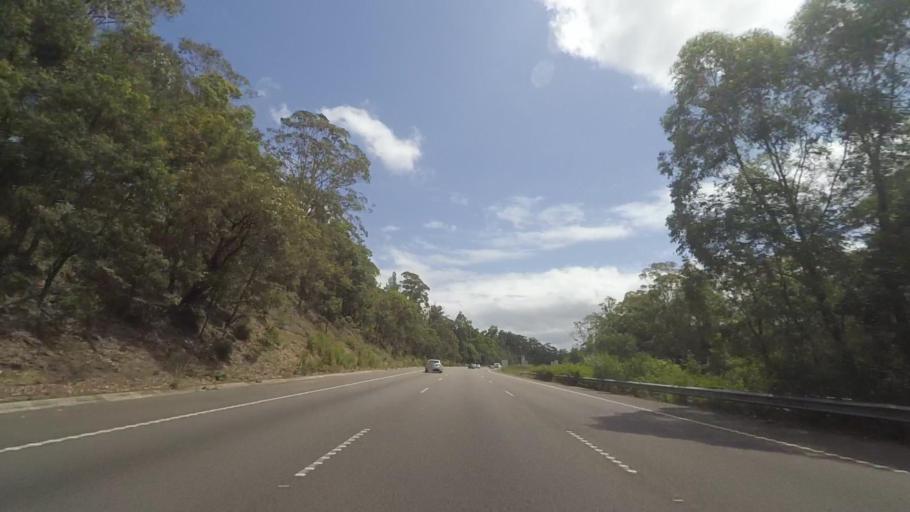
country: AU
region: New South Wales
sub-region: Gosford Shire
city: Lisarow
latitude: -33.3543
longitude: 151.3549
